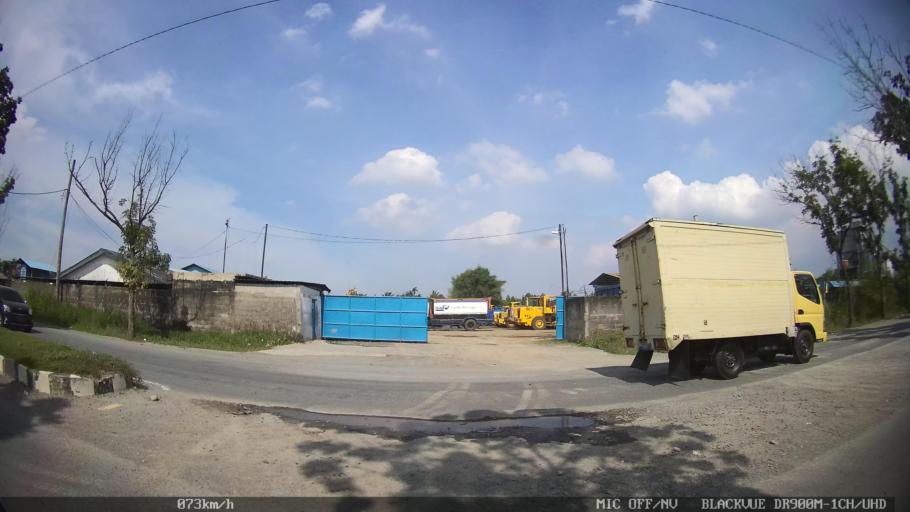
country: ID
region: North Sumatra
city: Binjai
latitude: 3.6317
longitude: 98.5352
